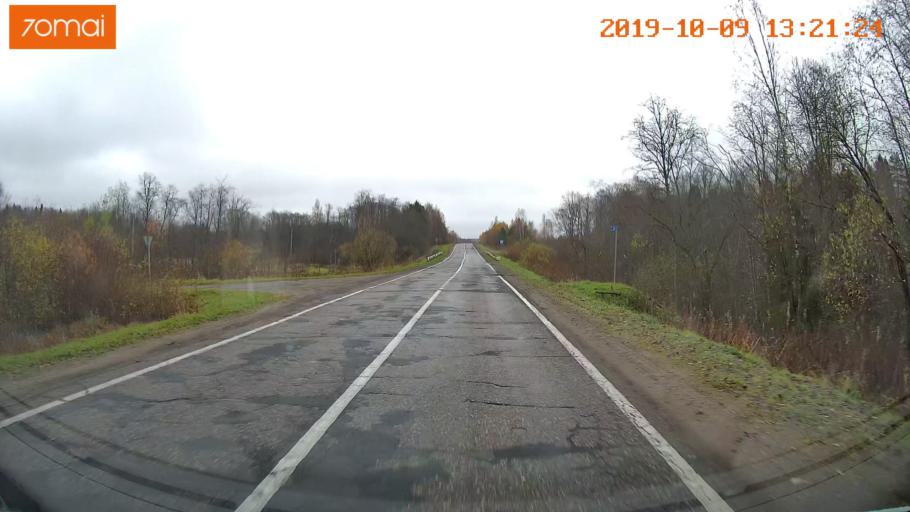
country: RU
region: Jaroslavl
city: Lyubim
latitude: 58.3407
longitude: 40.8458
